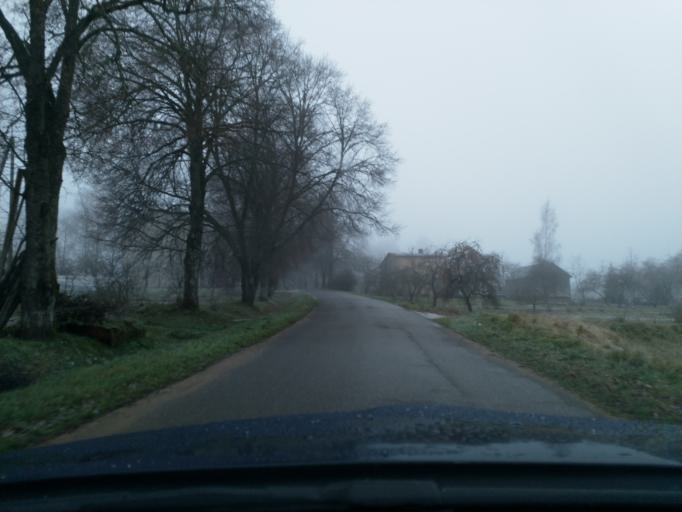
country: LV
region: Aizpute
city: Aizpute
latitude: 56.8359
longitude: 21.7751
